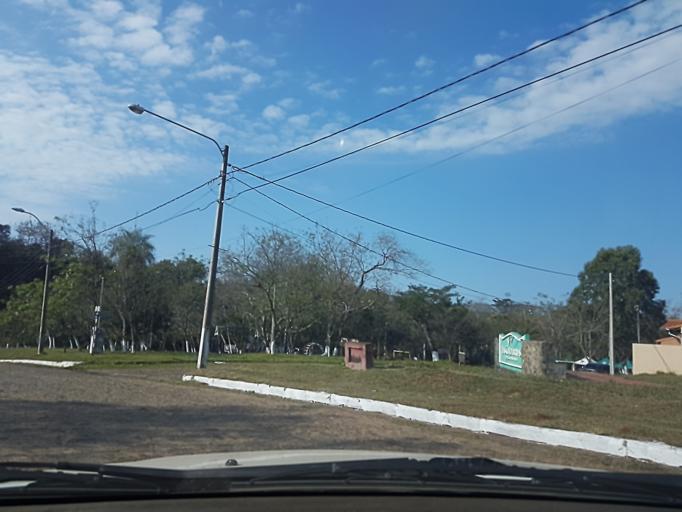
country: PY
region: Central
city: Colonia Mariano Roque Alonso
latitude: -25.2451
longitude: -57.5378
